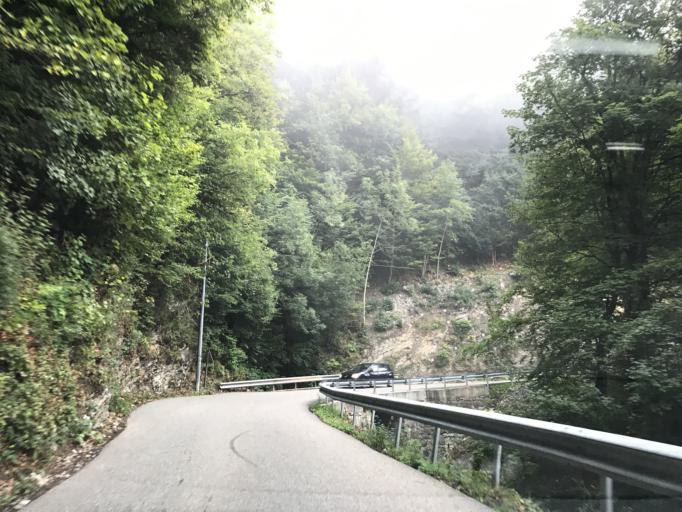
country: FR
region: Rhone-Alpes
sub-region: Departement de la Haute-Savoie
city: Talloires
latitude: 45.8171
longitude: 6.2441
